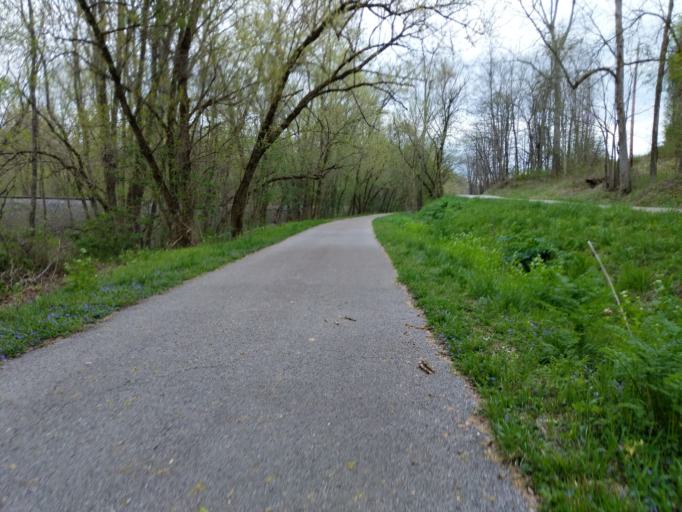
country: US
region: Ohio
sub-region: Athens County
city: Chauncey
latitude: 39.3860
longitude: -82.1197
